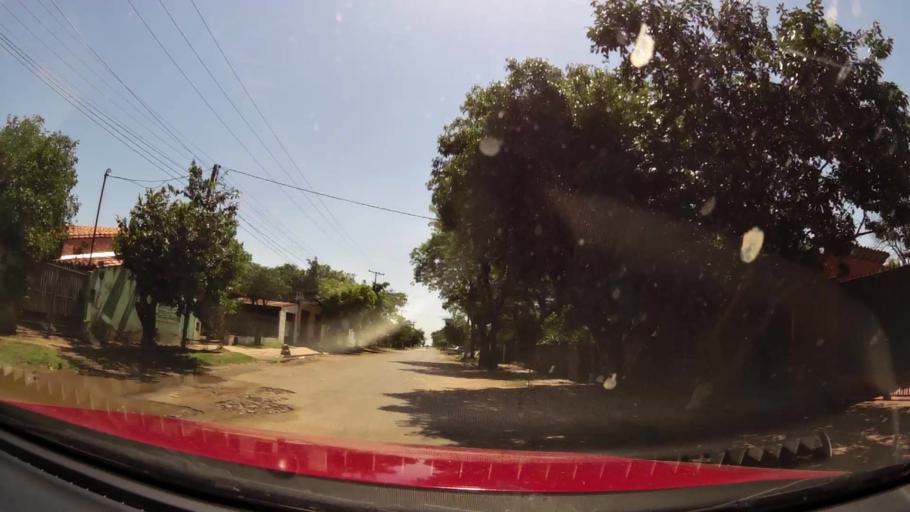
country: PY
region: Central
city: Colonia Mariano Roque Alonso
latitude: -25.2275
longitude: -57.5526
